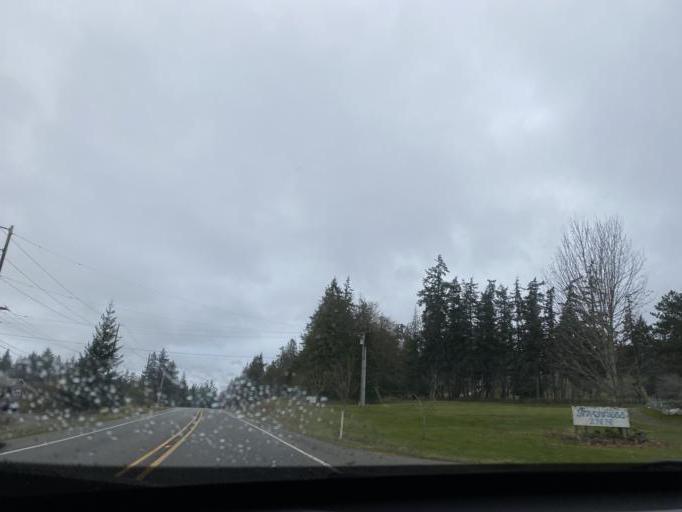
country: US
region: Washington
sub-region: Island County
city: Freeland
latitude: 48.0078
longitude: -122.4792
